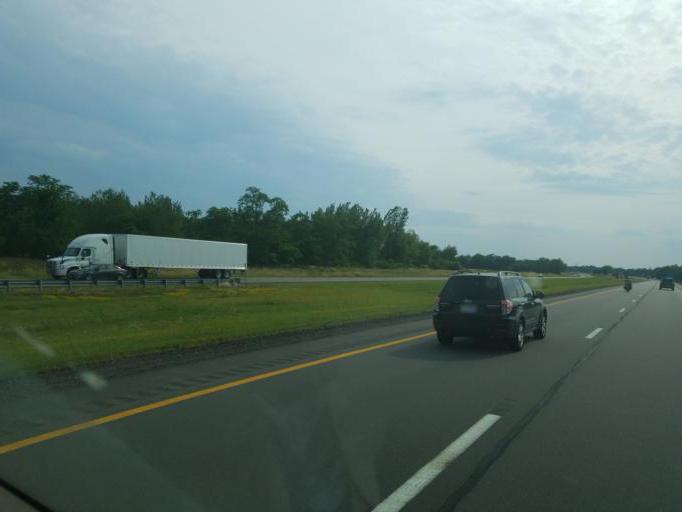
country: US
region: Pennsylvania
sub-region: Erie County
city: North East
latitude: 42.2749
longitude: -79.7172
